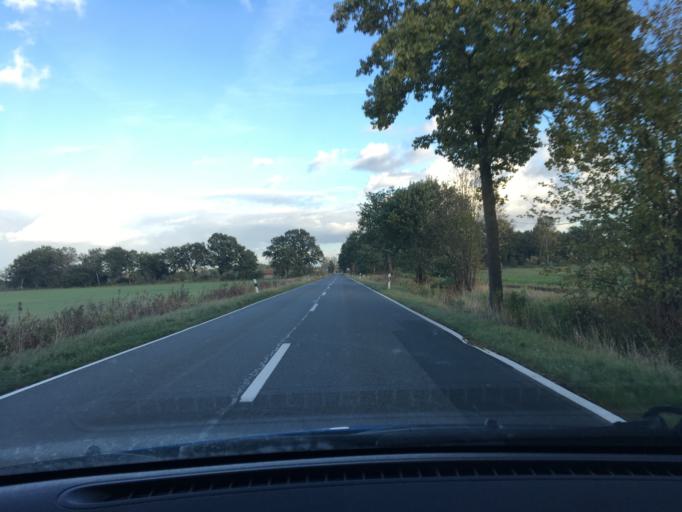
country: DE
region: Lower Saxony
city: Hittbergen
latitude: 53.3166
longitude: 10.6205
